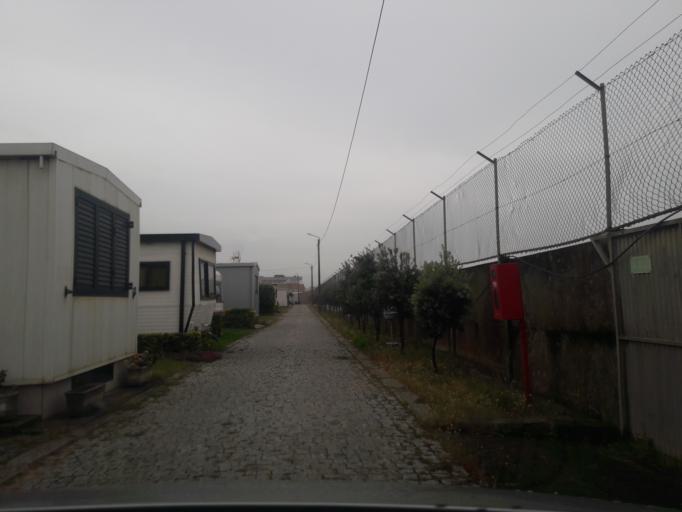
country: PT
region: Porto
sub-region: Vila do Conde
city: Vila do Conde
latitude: 41.3364
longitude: -8.7395
